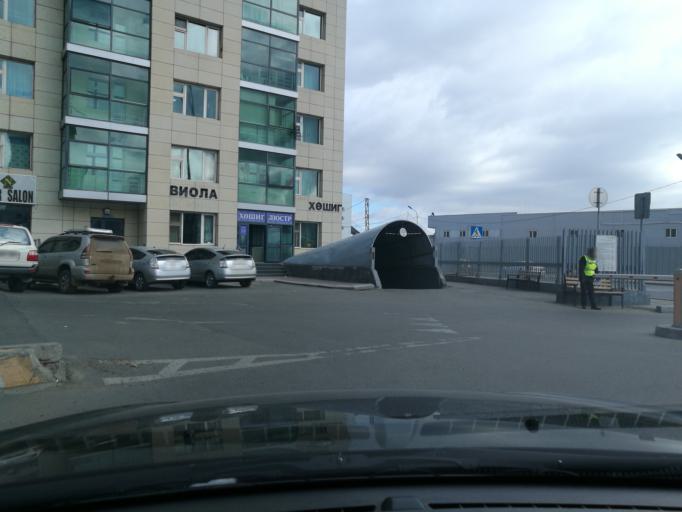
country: MN
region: Ulaanbaatar
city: Ulaanbaatar
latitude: 47.9045
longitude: 106.9135
